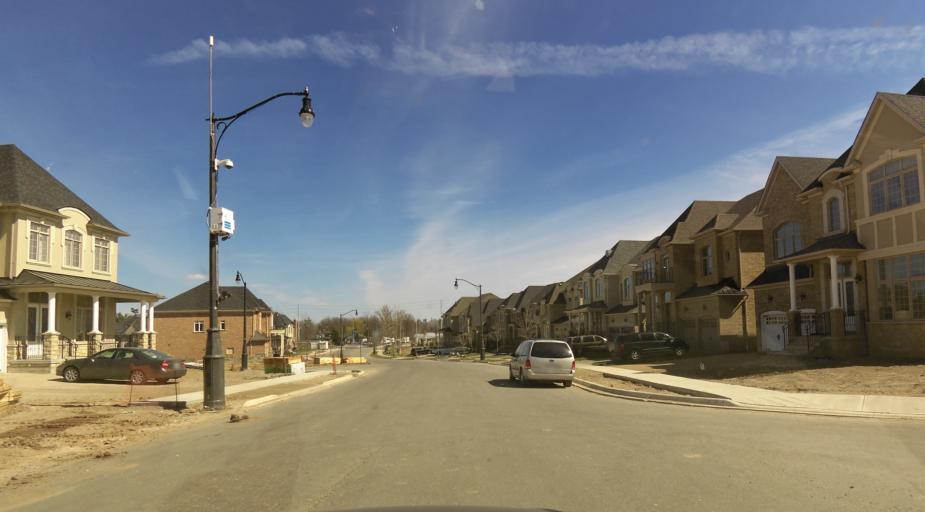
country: CA
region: Ontario
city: Brampton
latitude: 43.6508
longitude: -79.8027
